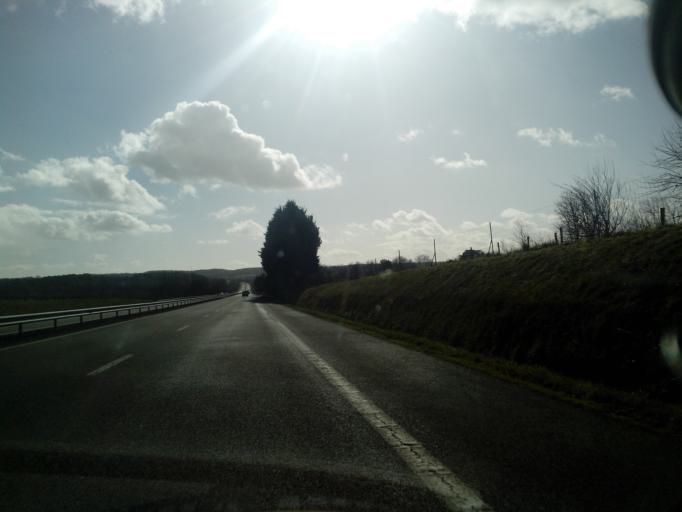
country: FR
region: Brittany
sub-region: Departement du Morbihan
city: Malestroit
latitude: 47.8422
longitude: -2.4251
